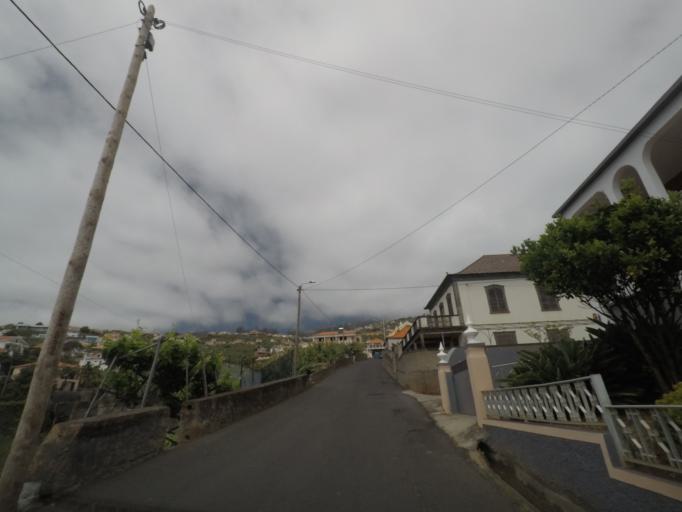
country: PT
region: Madeira
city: Ponta do Sol
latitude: 32.6890
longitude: -17.1009
